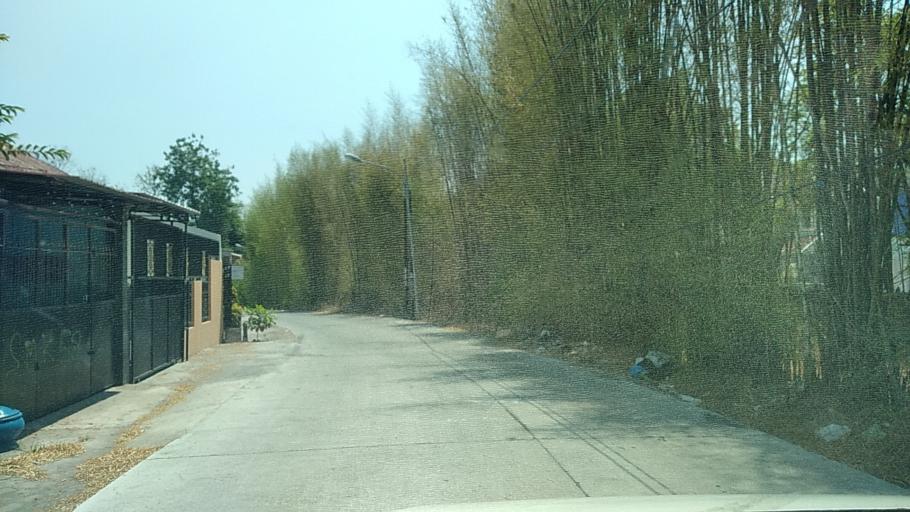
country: ID
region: Central Java
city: Semarang
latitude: -7.0225
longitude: 110.3758
